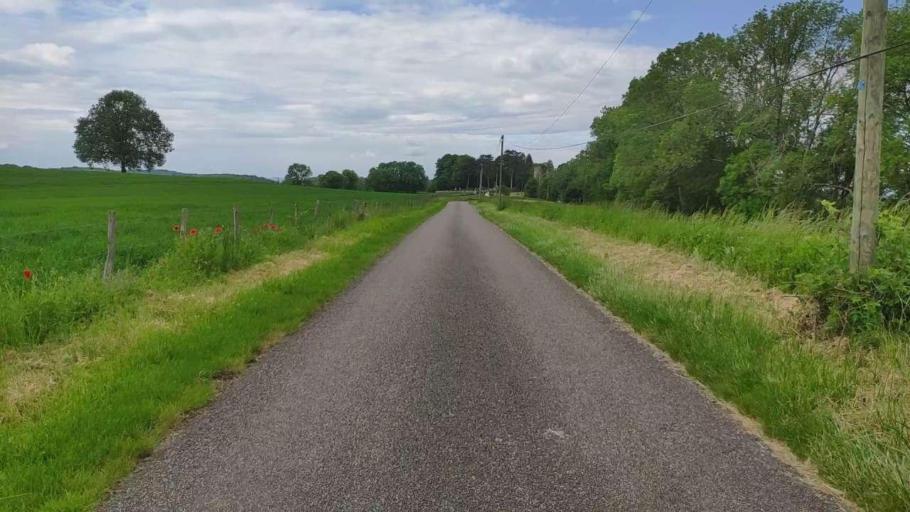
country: FR
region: Franche-Comte
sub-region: Departement du Jura
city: Perrigny
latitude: 46.7577
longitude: 5.6339
